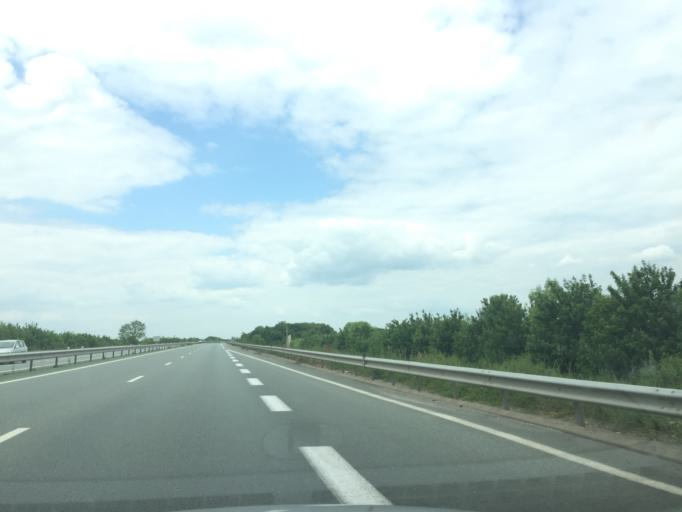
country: FR
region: Poitou-Charentes
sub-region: Departement des Deux-Sevres
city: Chauray
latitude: 46.3582
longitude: -0.3409
